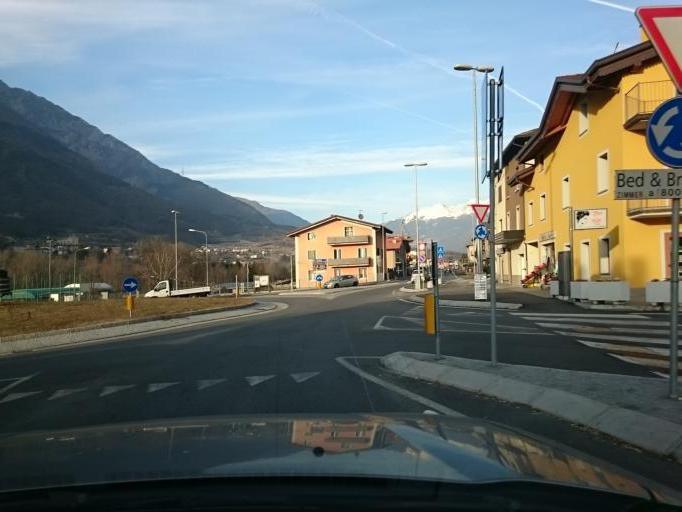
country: IT
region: Lombardy
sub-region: Provincia di Brescia
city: Losine
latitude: 45.9764
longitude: 10.3214
